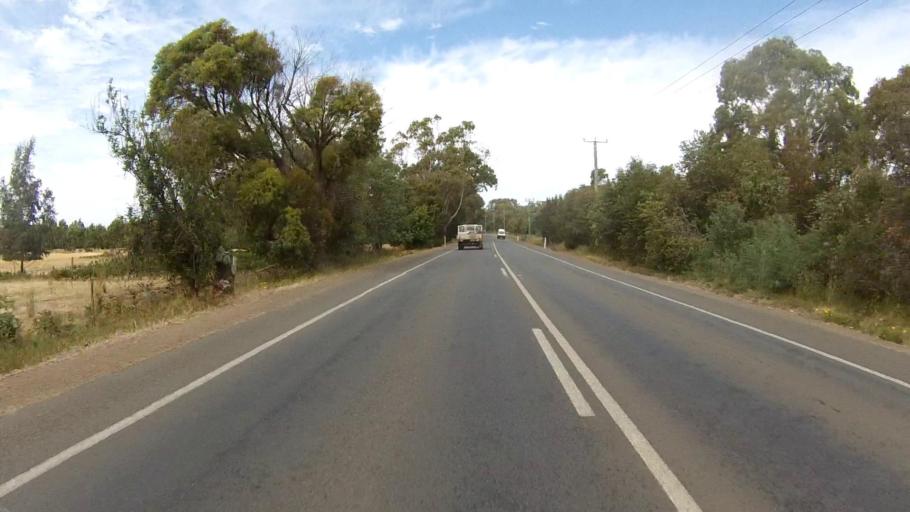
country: AU
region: Tasmania
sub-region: Clarence
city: Sandford
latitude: -42.9414
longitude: 147.4975
